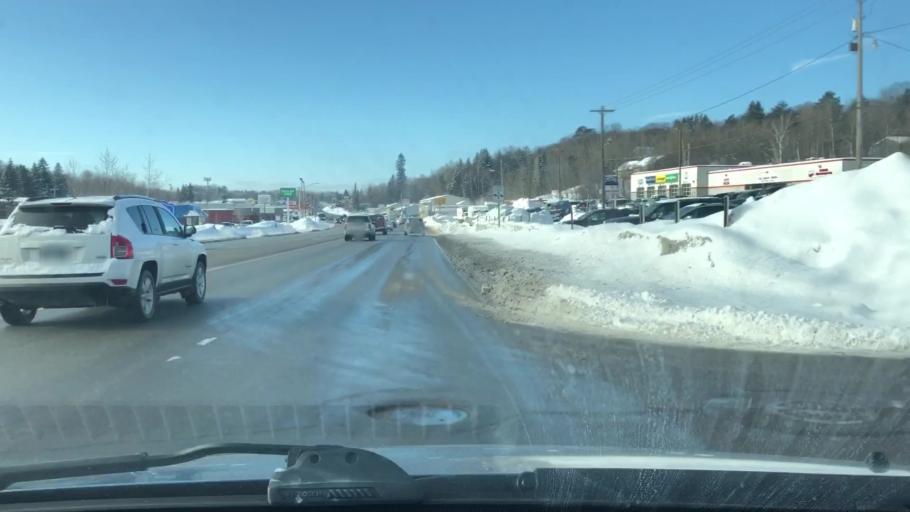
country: US
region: Minnesota
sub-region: Saint Louis County
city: Duluth
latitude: 46.8002
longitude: -92.1217
